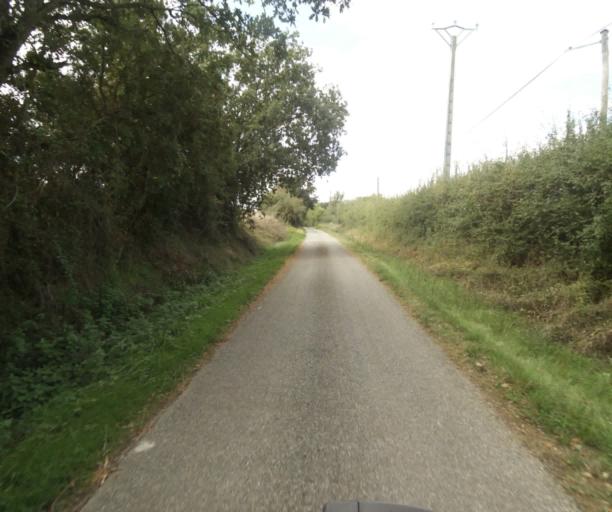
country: FR
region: Midi-Pyrenees
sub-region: Departement du Tarn-et-Garonne
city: Saint-Porquier
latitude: 43.9542
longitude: 1.1518
